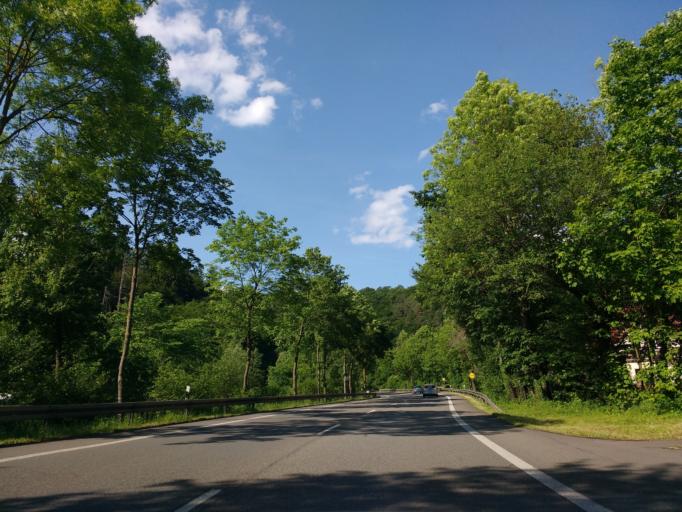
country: DE
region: Hesse
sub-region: Regierungsbezirk Kassel
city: Vohl
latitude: 51.2221
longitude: 8.8945
